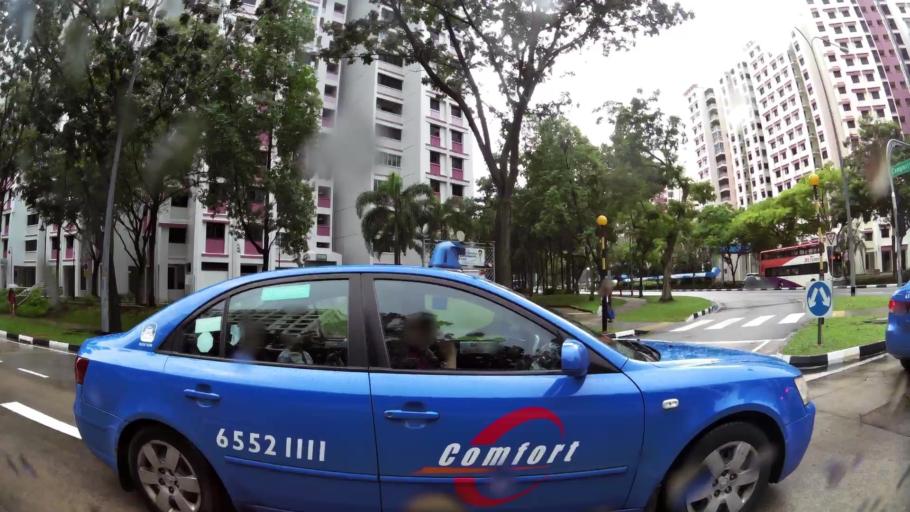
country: MY
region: Johor
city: Kampung Pasir Gudang Baru
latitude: 1.3879
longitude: 103.8968
